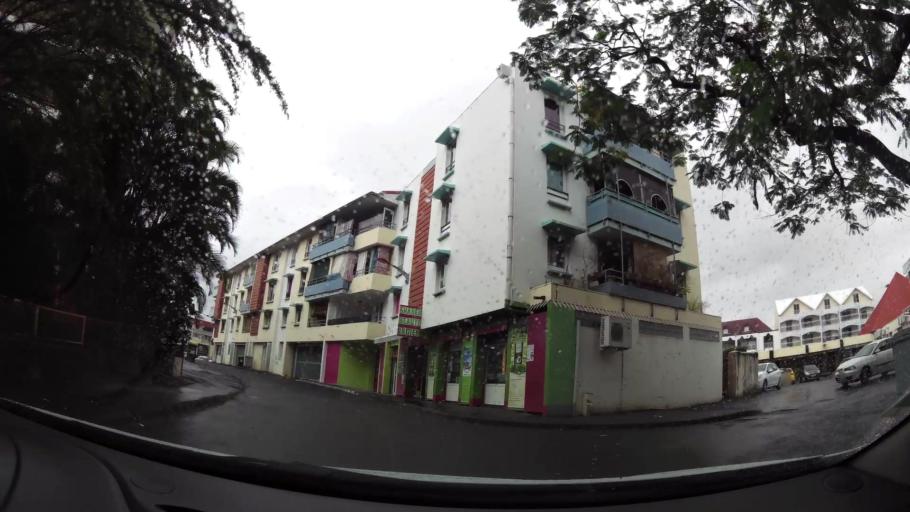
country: RE
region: Reunion
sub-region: Reunion
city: Saint-Andre
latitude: -20.9606
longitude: 55.6517
